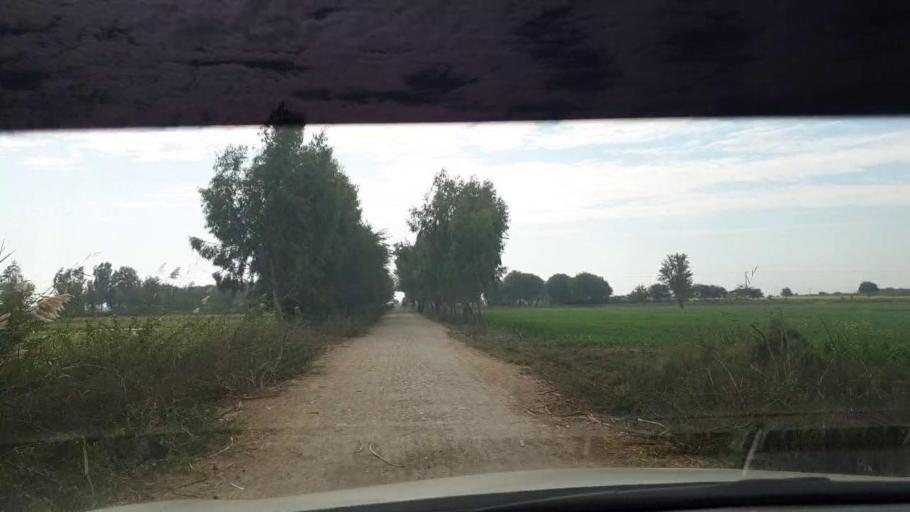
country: PK
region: Sindh
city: Berani
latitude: 25.7286
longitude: 68.8658
